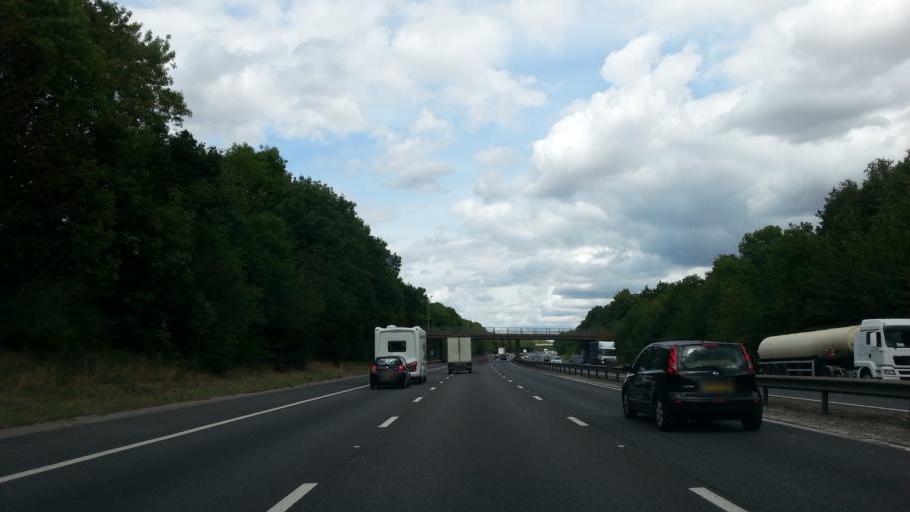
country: GB
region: England
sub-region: Essex
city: Harlow
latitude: 51.7559
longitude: 0.1465
